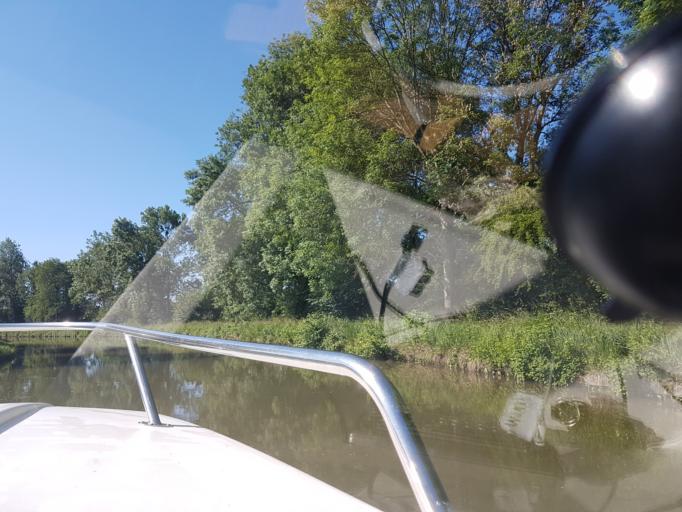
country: FR
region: Bourgogne
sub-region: Departement de la Nievre
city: Clamecy
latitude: 47.5351
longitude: 3.5995
